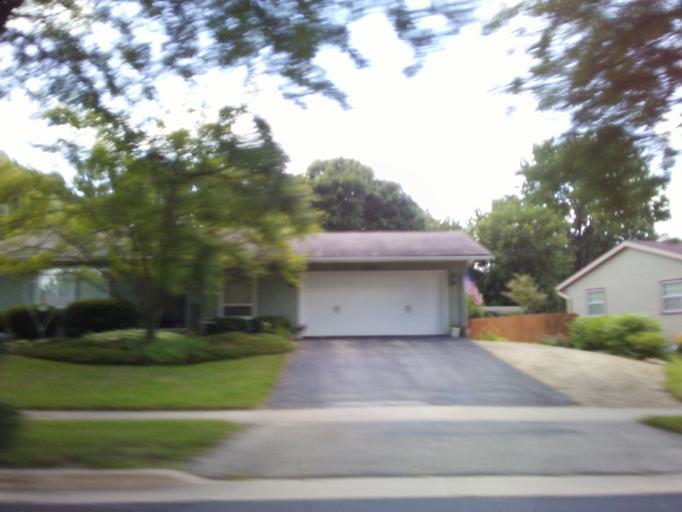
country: US
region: Wisconsin
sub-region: Dane County
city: Verona
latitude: 43.0223
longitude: -89.5027
